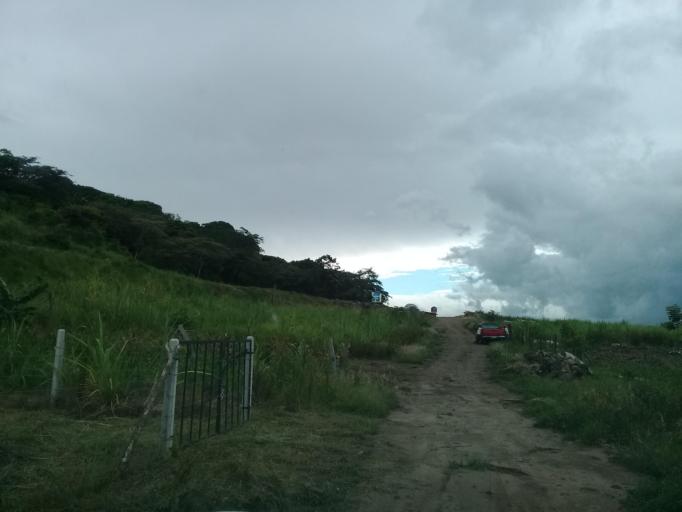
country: MX
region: Veracruz
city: El Castillo
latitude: 19.5633
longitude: -96.8430
